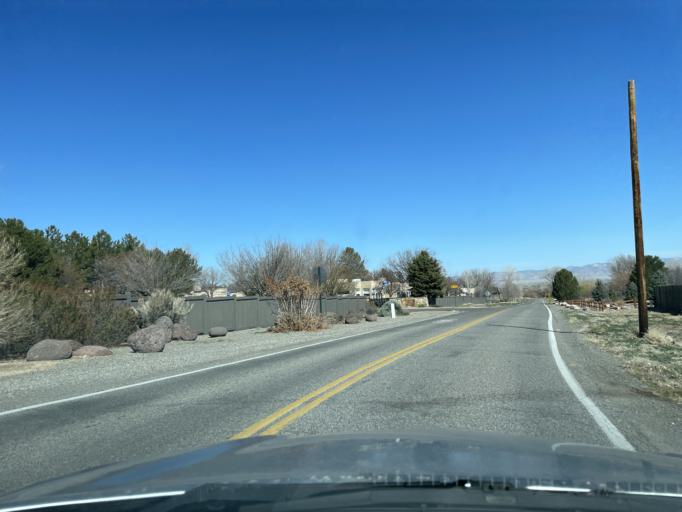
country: US
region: Colorado
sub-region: Mesa County
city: Redlands
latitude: 39.0745
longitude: -108.6641
